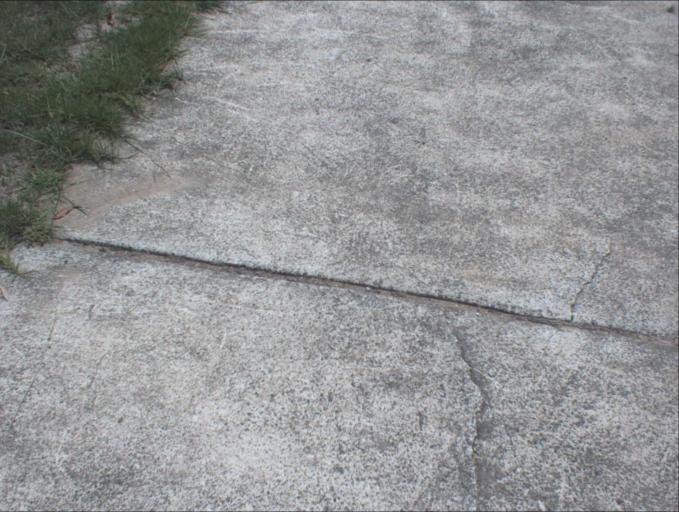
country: AU
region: Queensland
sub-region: Logan
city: Windaroo
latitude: -27.7394
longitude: 153.1857
